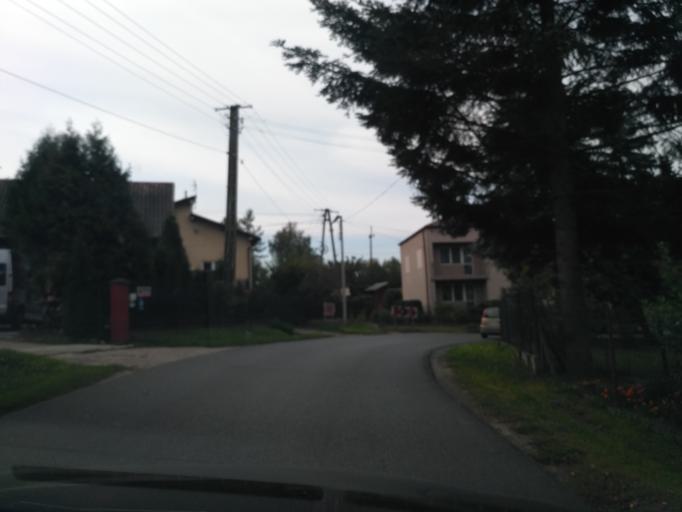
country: PL
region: Subcarpathian Voivodeship
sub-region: Powiat rzeszowski
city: Zglobien
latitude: 50.0085
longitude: 21.8582
